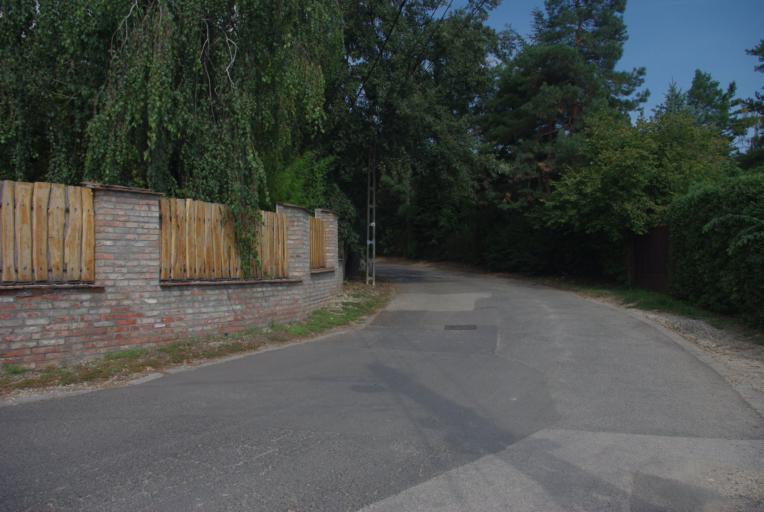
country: HU
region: Pest
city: Budaors
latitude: 47.4840
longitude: 18.9781
